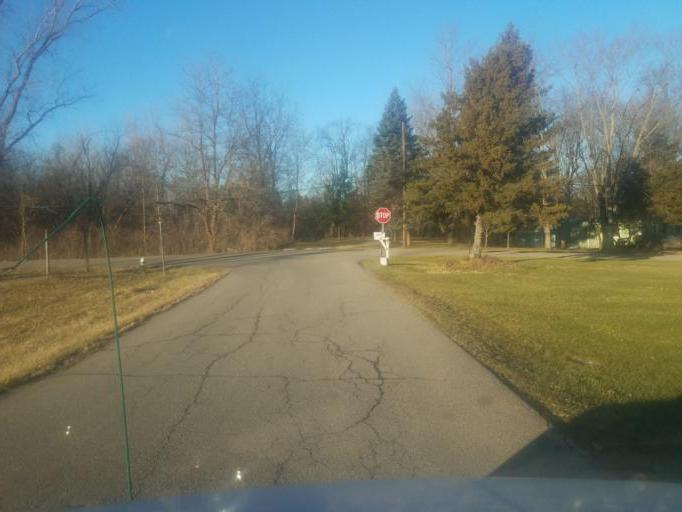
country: US
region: Ohio
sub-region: Richland County
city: Mansfield
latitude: 40.7910
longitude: -82.5364
